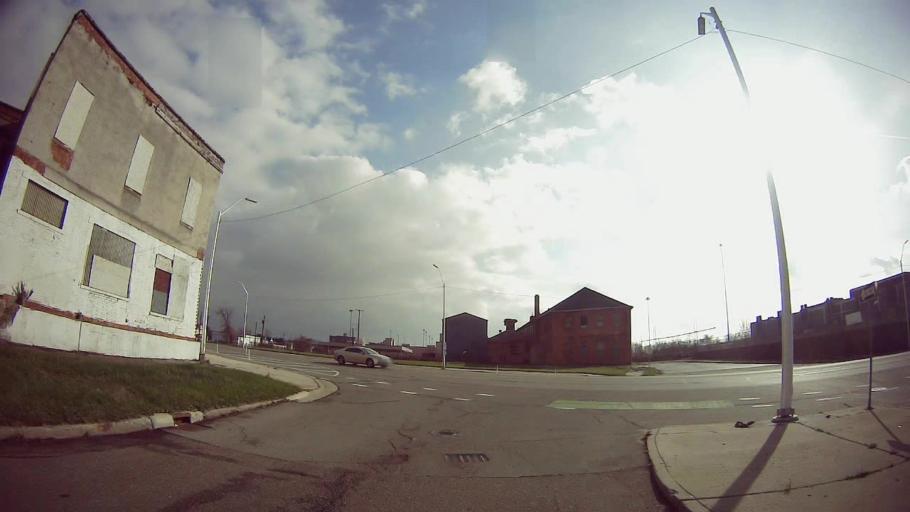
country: US
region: Michigan
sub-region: Wayne County
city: Detroit
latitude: 42.3315
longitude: -83.0984
